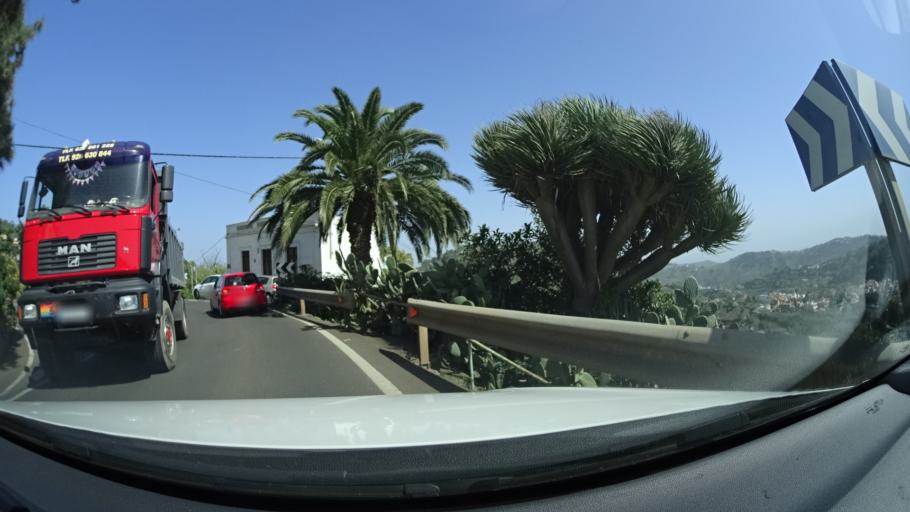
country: ES
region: Canary Islands
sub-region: Provincia de Las Palmas
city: Teror
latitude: 28.0833
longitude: -15.5407
